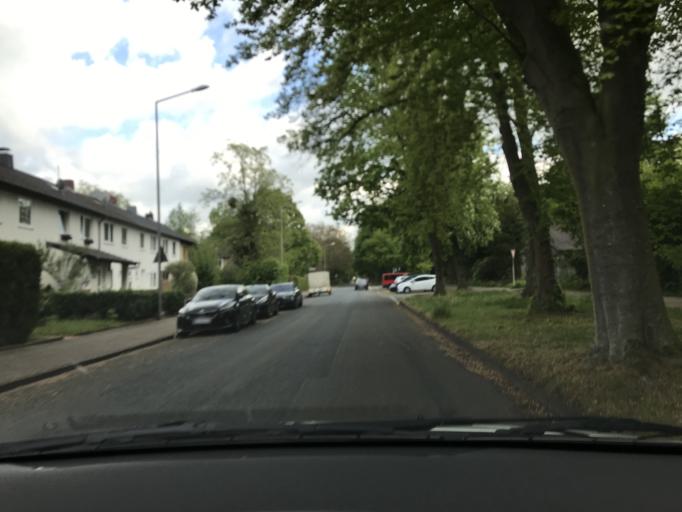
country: DE
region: North Rhine-Westphalia
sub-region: Regierungsbezirk Detmold
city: Minden
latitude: 52.2806
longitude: 8.8940
